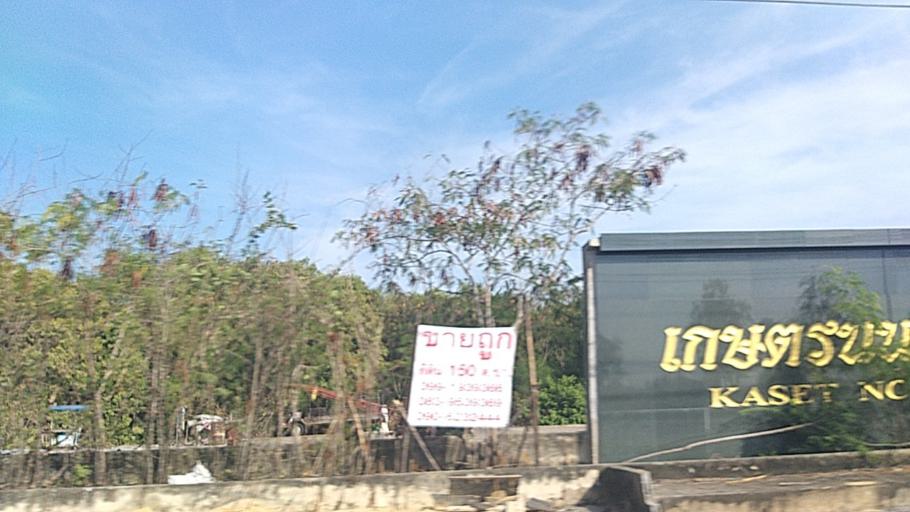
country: TH
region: Pathum Thani
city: Thanyaburi
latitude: 13.9770
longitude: 100.7289
